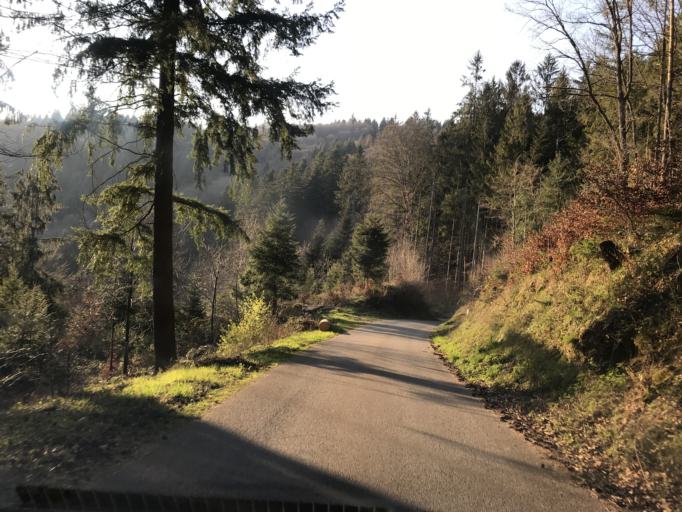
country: DE
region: Baden-Wuerttemberg
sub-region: Freiburg Region
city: Hausen
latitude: 47.6862
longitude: 7.8339
